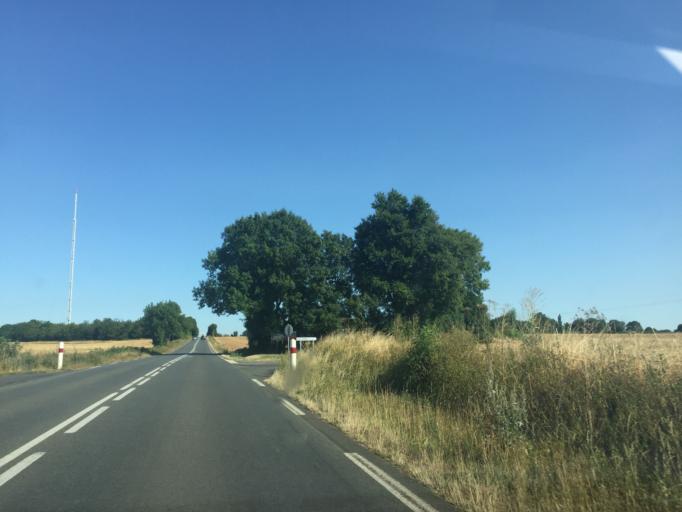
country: FR
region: Poitou-Charentes
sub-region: Departement des Deux-Sevres
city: Melle
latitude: 46.1958
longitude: -0.0694
